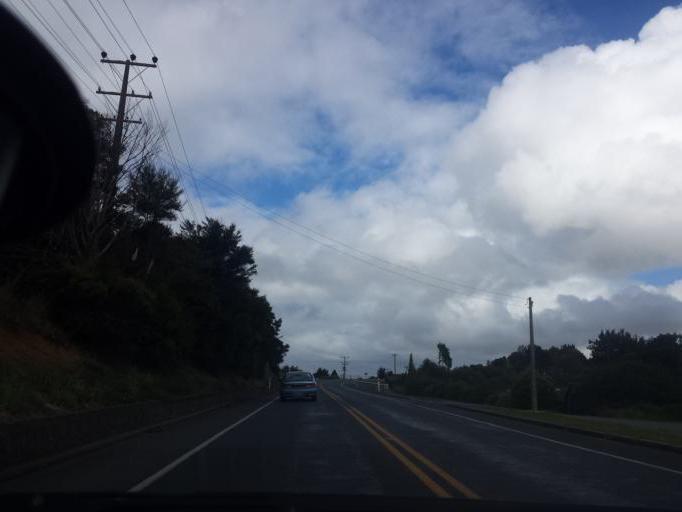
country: NZ
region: Auckland
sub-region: Auckland
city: Warkworth
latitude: -36.3996
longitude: 174.7096
